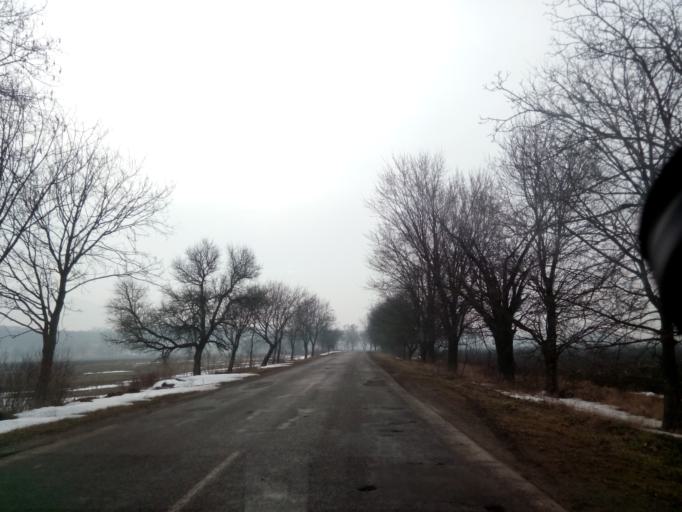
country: HU
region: Borsod-Abauj-Zemplen
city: Gonc
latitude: 48.4870
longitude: 21.2523
